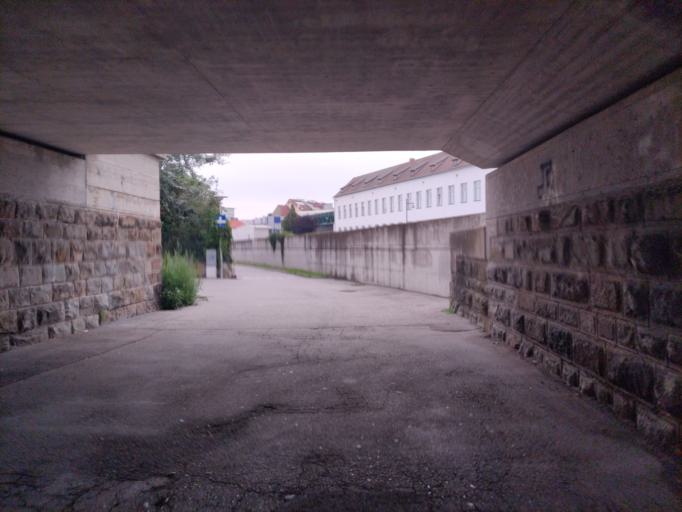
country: AT
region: Lower Austria
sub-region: Krems an der Donau Stadt
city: Krems an der Donau
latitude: 48.4109
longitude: 15.6085
